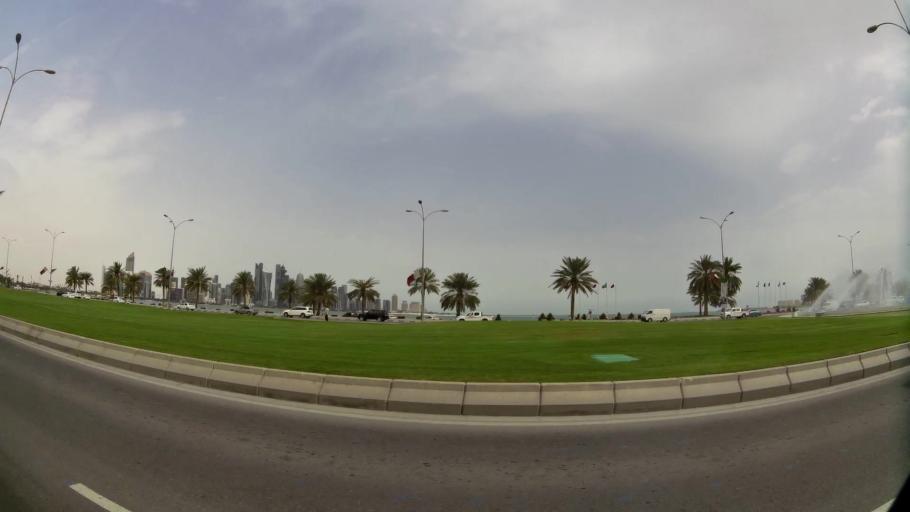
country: QA
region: Baladiyat ad Dawhah
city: Doha
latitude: 25.2958
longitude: 51.5217
